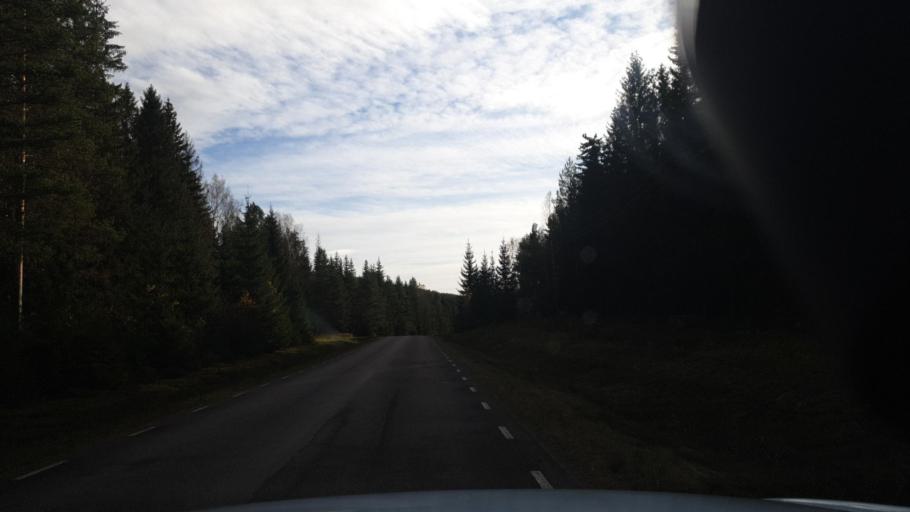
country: SE
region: Vaermland
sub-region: Eda Kommun
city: Charlottenberg
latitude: 59.9491
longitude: 12.3855
